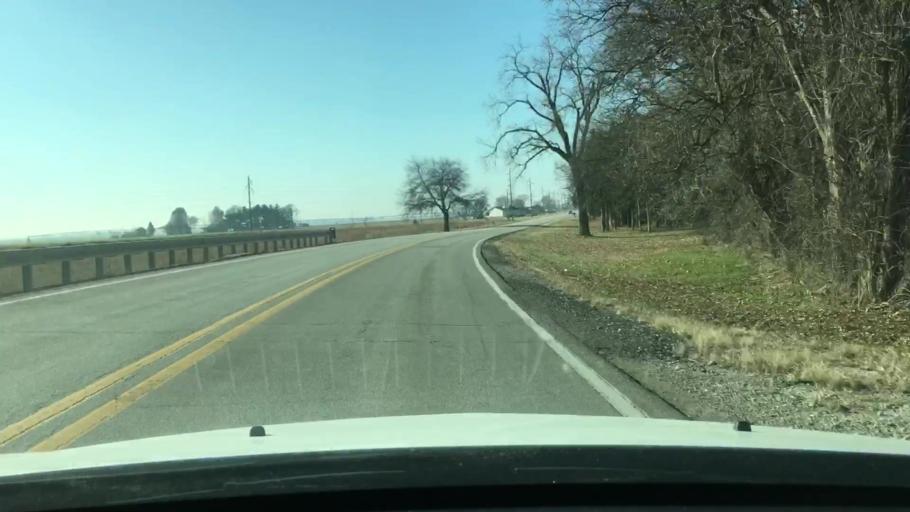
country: US
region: Illinois
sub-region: Cass County
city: Beardstown
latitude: 39.9902
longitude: -90.4385
